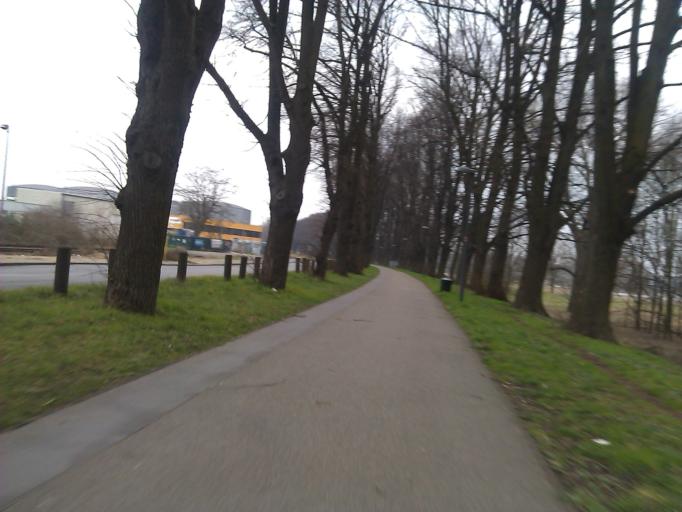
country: DE
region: North Rhine-Westphalia
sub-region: Regierungsbezirk Koln
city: Muelheim
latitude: 50.9756
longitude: 6.9904
